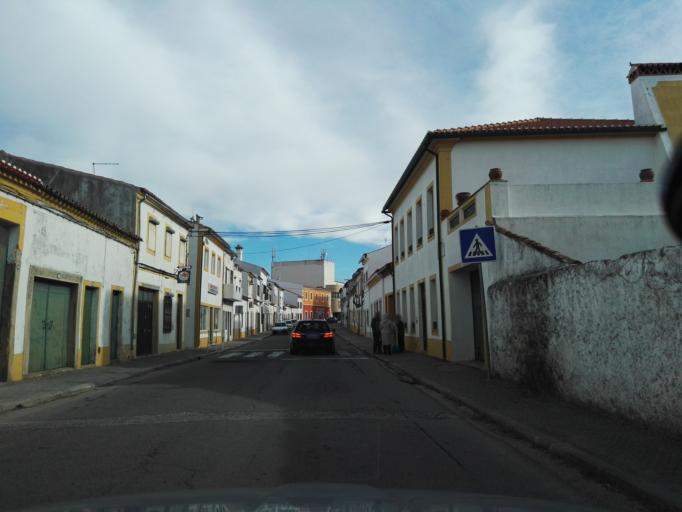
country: PT
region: Portalegre
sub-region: Nisa
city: Nisa
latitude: 39.5155
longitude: -7.6524
